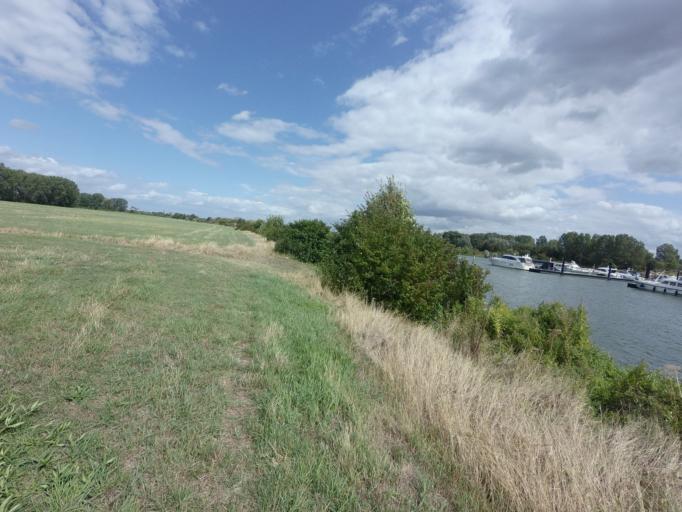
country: NL
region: Limburg
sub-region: Gemeente Maasgouw
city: Maasbracht
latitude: 51.1407
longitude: 5.8697
